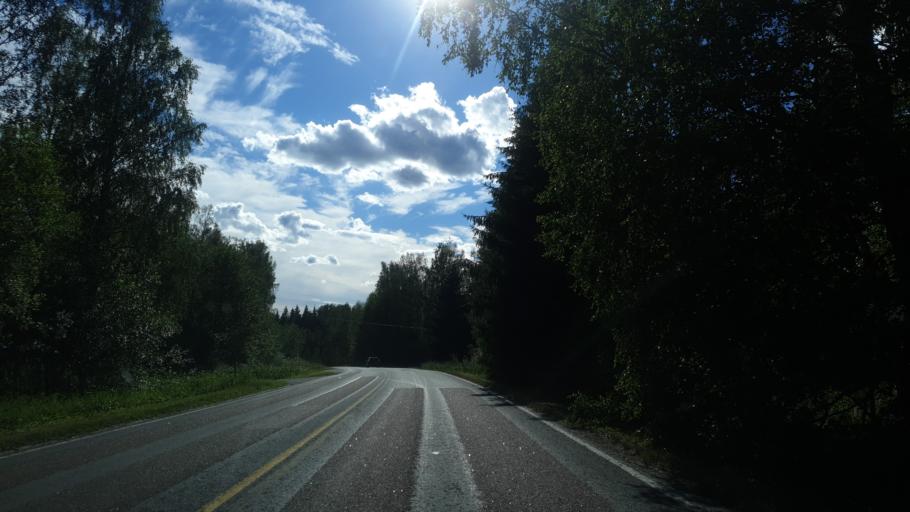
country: FI
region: Southern Savonia
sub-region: Mikkeli
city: Pertunmaa
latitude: 61.5232
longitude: 26.5102
